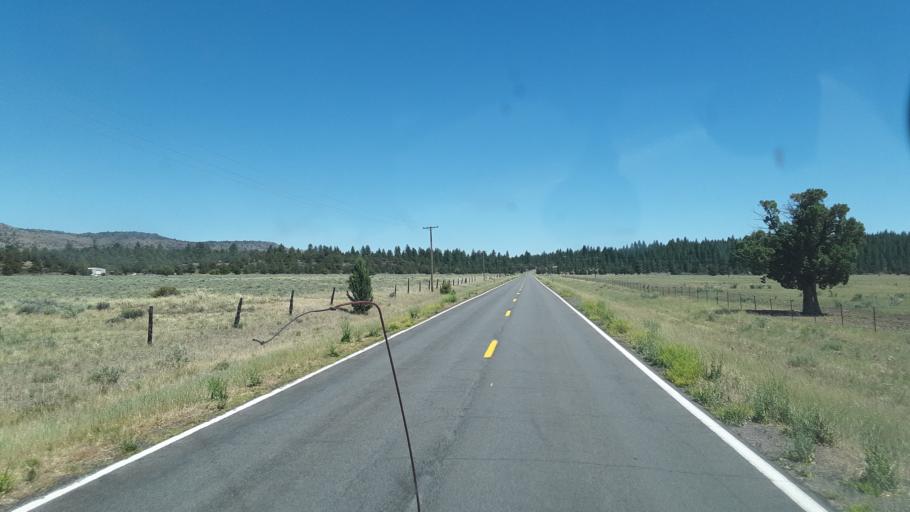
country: US
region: California
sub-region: Lassen County
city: Susanville
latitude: 40.5210
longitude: -120.5876
